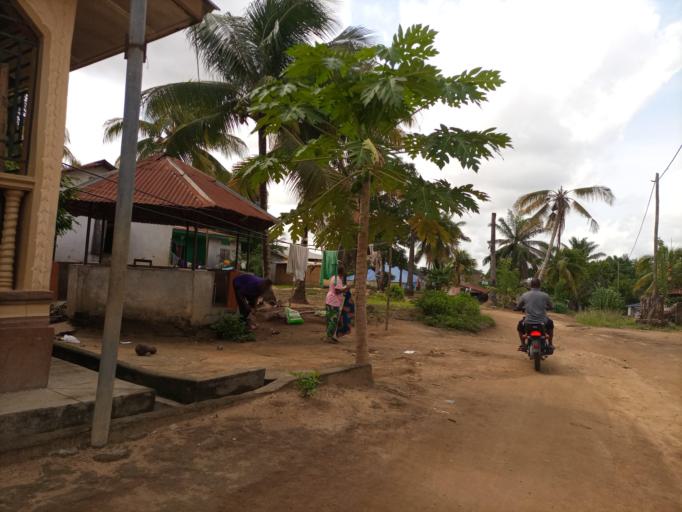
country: SL
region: Southern Province
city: Bo
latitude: 7.9616
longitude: -11.7604
